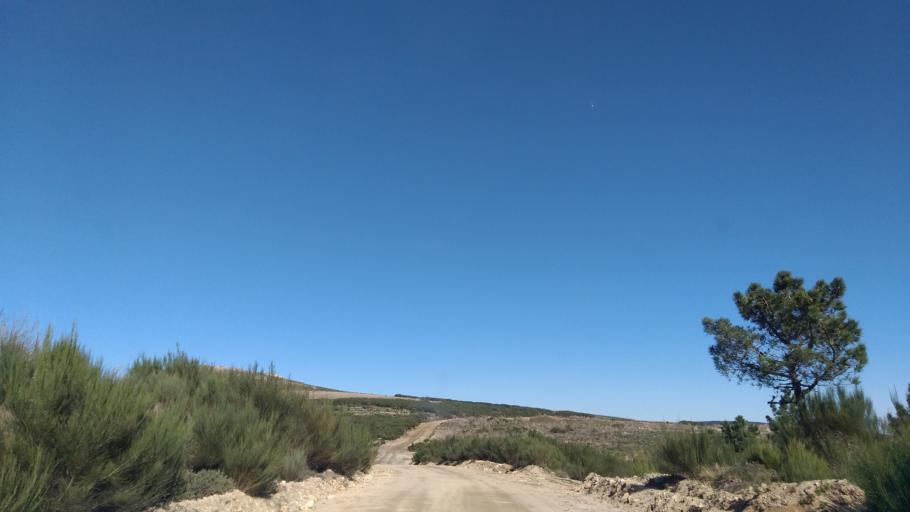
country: PT
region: Guarda
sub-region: Manteigas
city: Manteigas
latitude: 40.5027
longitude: -7.4884
